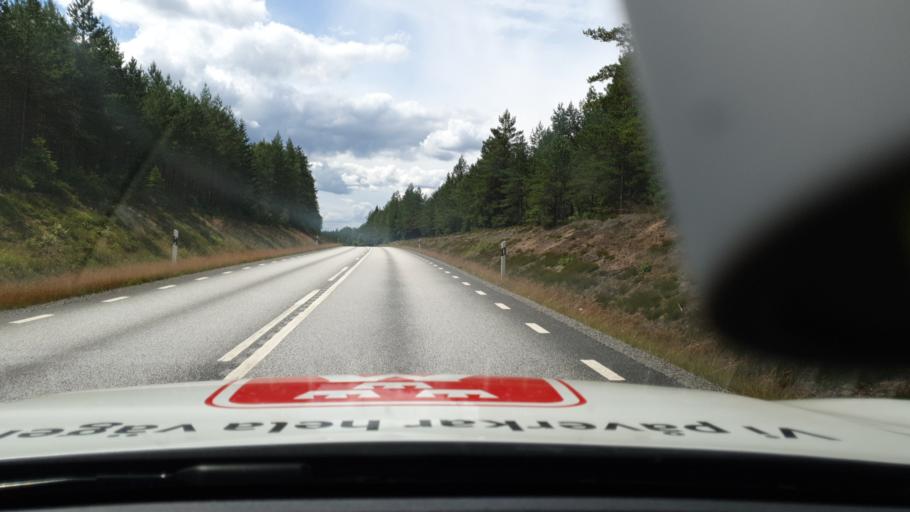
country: SE
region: Joenkoeping
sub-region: Gnosjo Kommun
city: Gnosjoe
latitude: 57.5682
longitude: 13.7058
